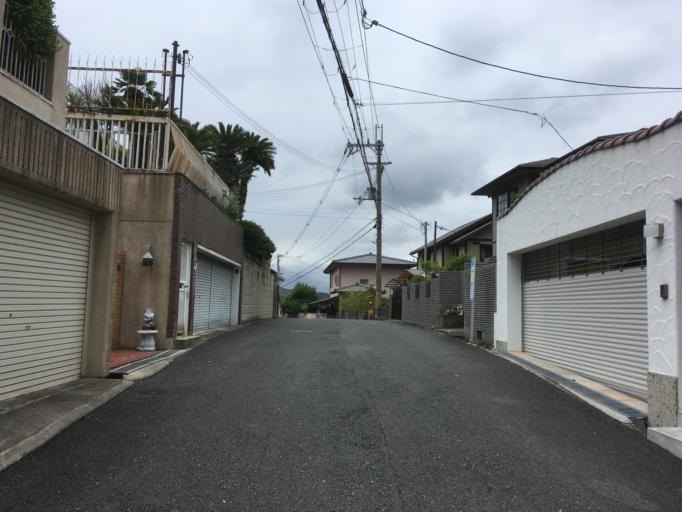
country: JP
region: Nara
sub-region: Ikoma-shi
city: Ikoma
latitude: 34.6949
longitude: 135.6930
